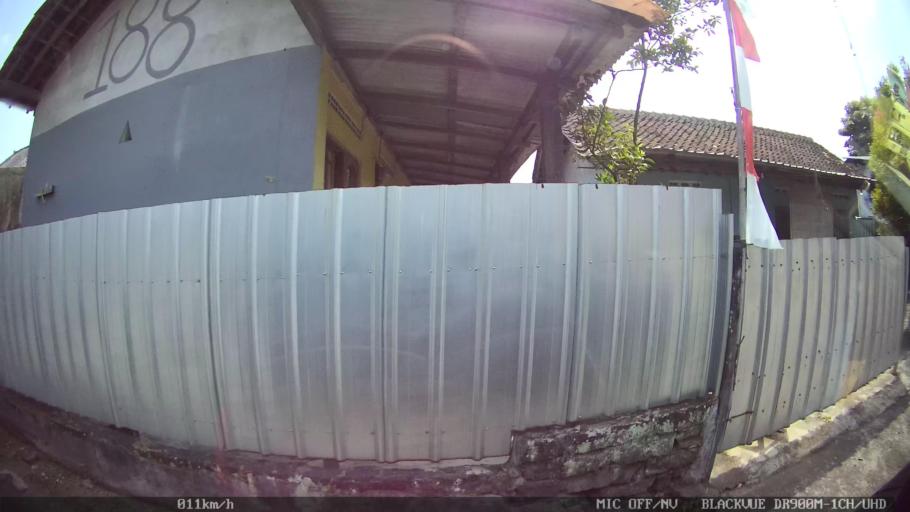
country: ID
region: Daerah Istimewa Yogyakarta
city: Yogyakarta
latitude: -7.8046
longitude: 110.3846
